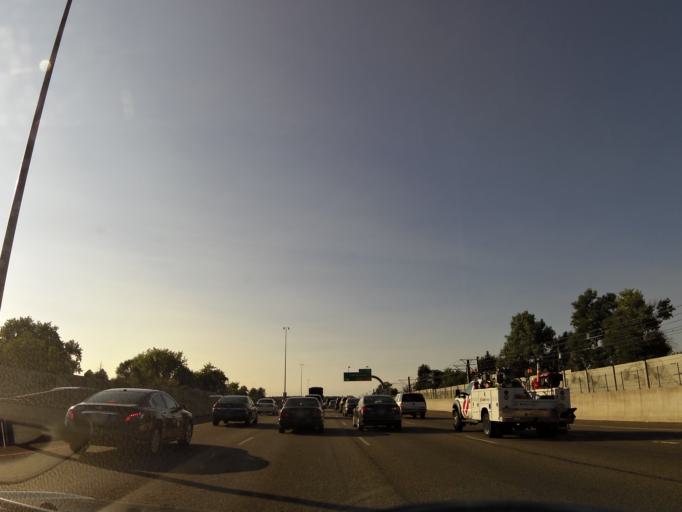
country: US
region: Colorado
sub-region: Arapahoe County
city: Glendale
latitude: 39.6729
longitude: -104.9293
